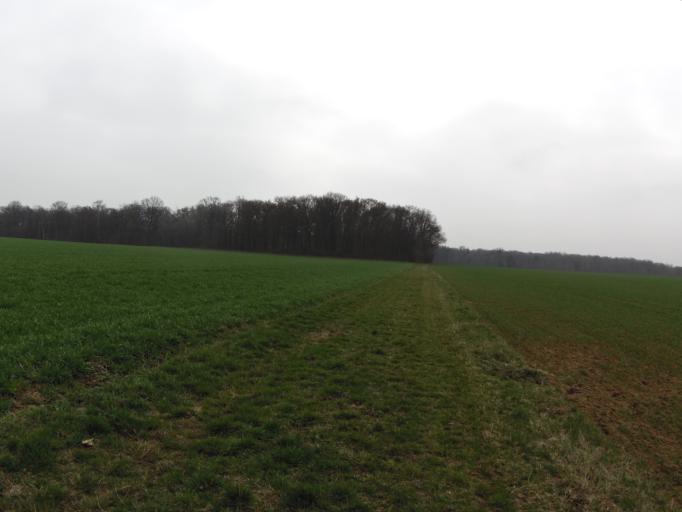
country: DE
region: Bavaria
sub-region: Regierungsbezirk Unterfranken
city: Rottendorf
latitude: 49.8185
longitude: 10.0329
